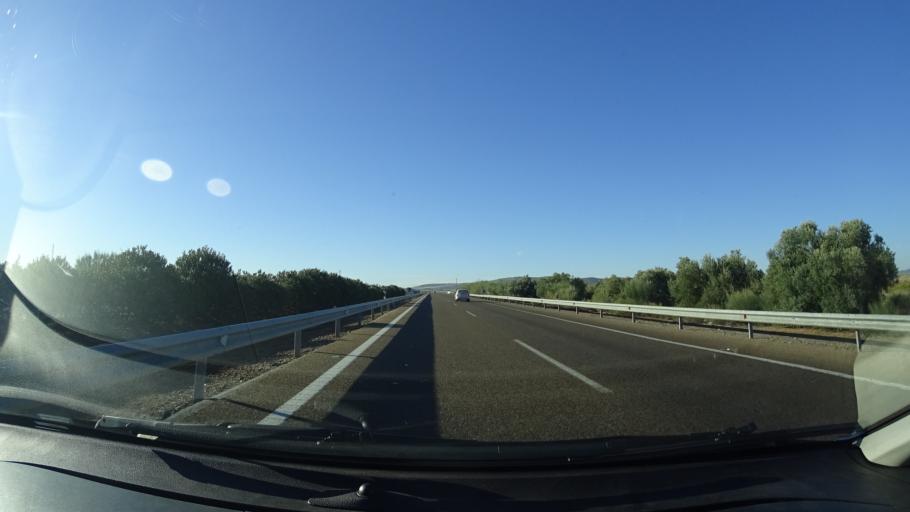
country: ES
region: Extremadura
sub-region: Provincia de Badajoz
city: Villafranca de los Barros
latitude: 38.5532
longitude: -6.3636
